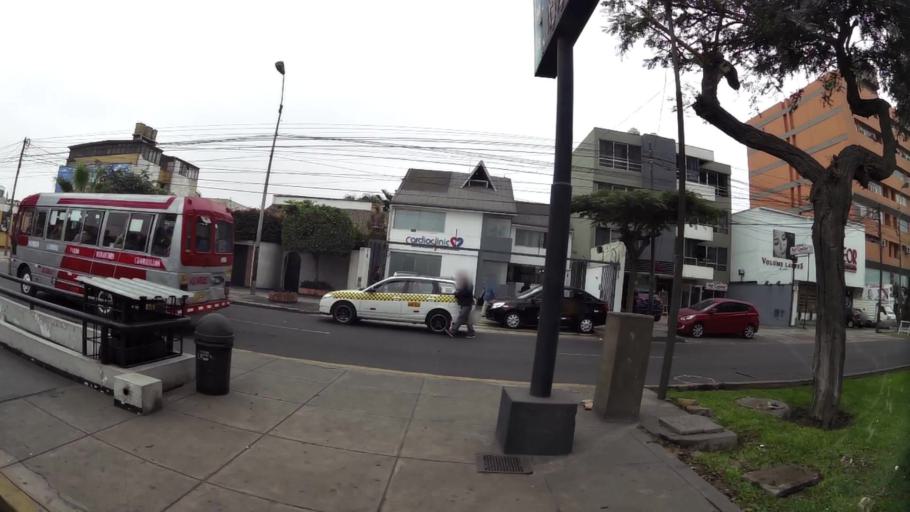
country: PE
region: Lima
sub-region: Lima
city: Surco
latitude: -12.1275
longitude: -77.0104
